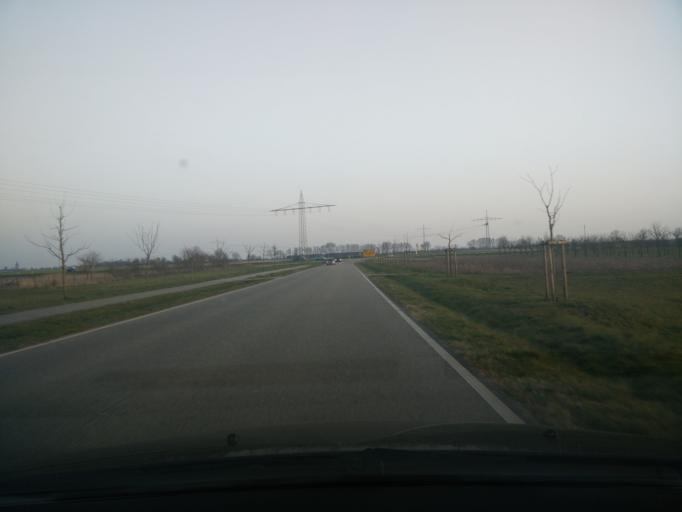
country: DE
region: Rheinland-Pfalz
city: Kandel
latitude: 49.0955
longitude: 8.1720
